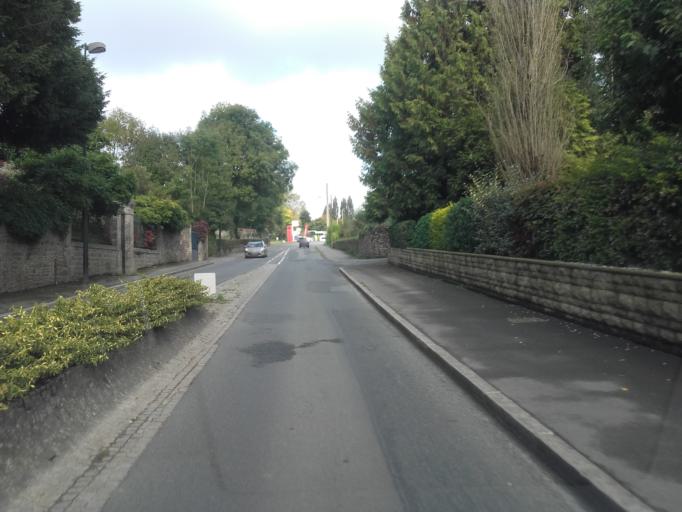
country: FR
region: Brittany
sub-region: Departement des Cotes-d'Armor
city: Plelo
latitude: 48.5439
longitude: -2.9666
